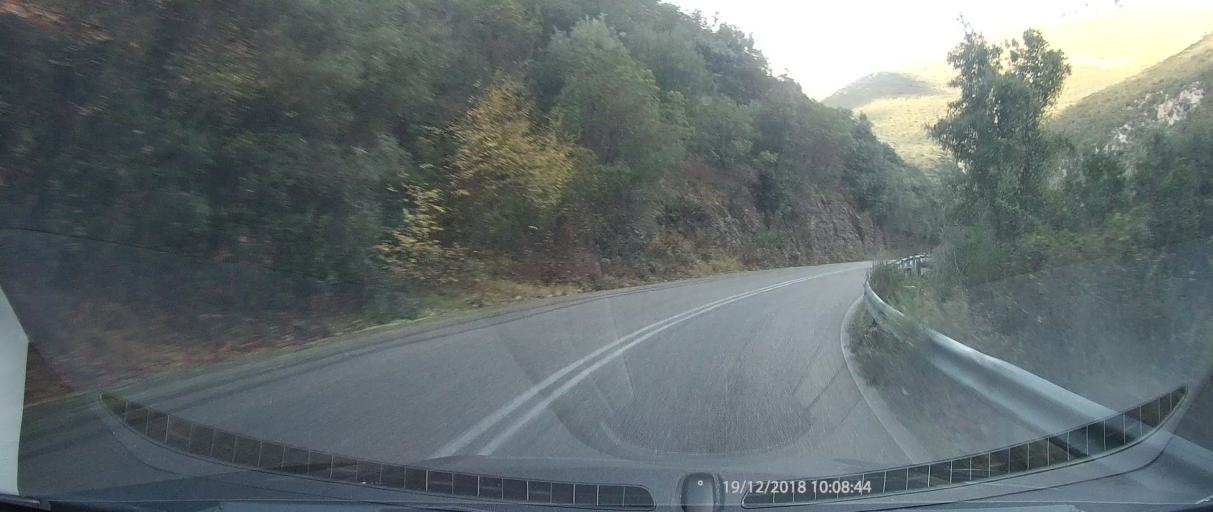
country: GR
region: Peloponnese
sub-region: Nomos Messinias
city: Kalamata
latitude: 37.1137
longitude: 22.1989
